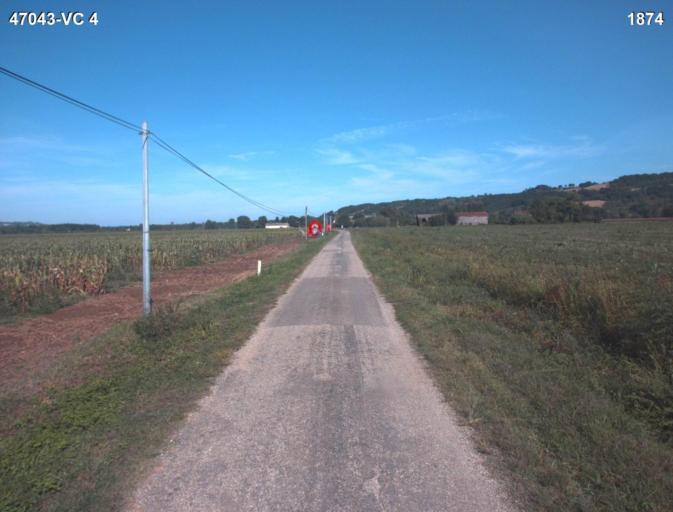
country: FR
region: Aquitaine
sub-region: Departement du Lot-et-Garonne
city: Buzet-sur-Baise
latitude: 44.2700
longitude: 0.3221
